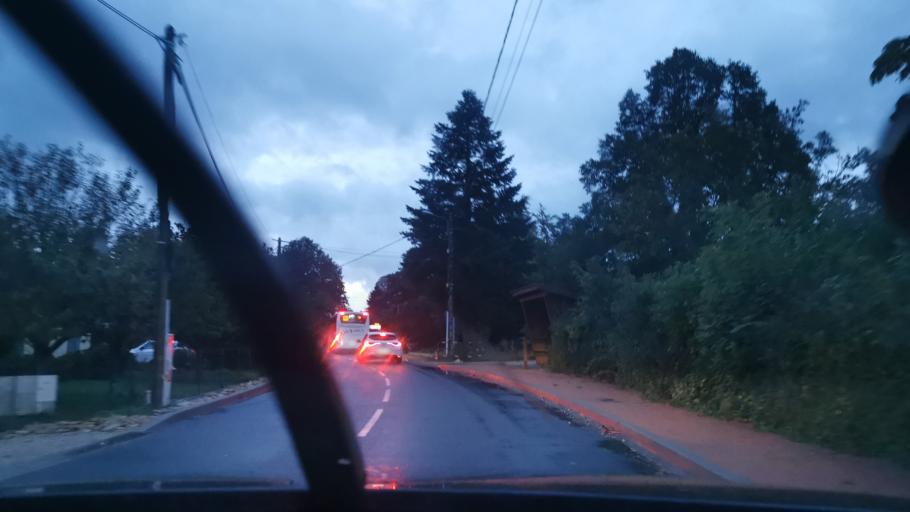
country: FR
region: Rhone-Alpes
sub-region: Departement de l'Ain
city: Crottet
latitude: 46.2728
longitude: 4.8978
